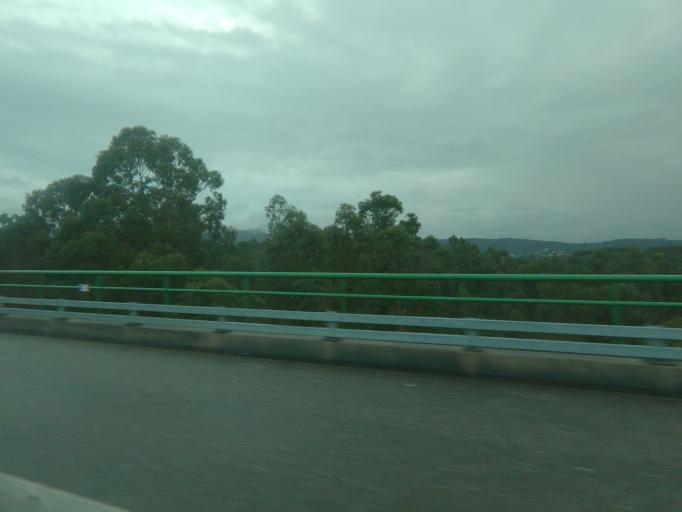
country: PT
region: Viana do Castelo
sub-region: Valenca
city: Valenza
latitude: 41.9761
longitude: -8.6579
